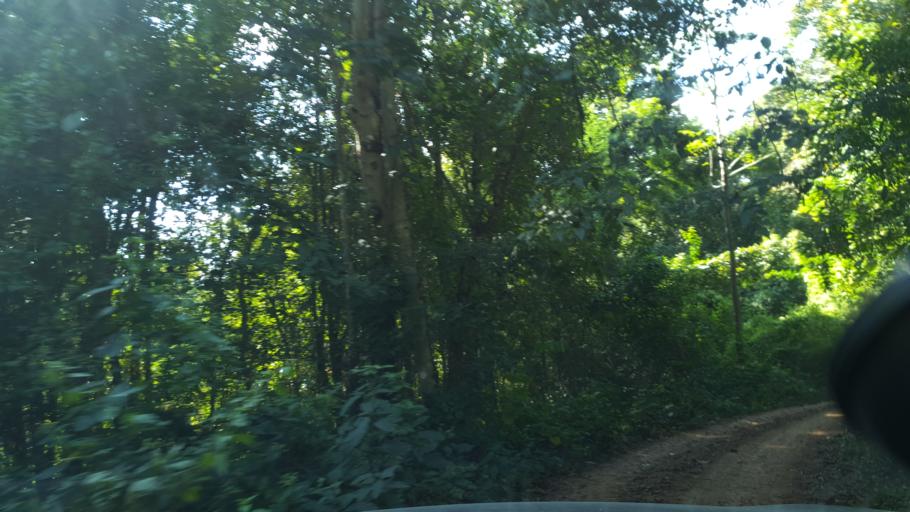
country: TH
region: Chiang Mai
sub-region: Amphoe Chiang Dao
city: Chiang Dao
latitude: 19.3197
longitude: 98.7269
